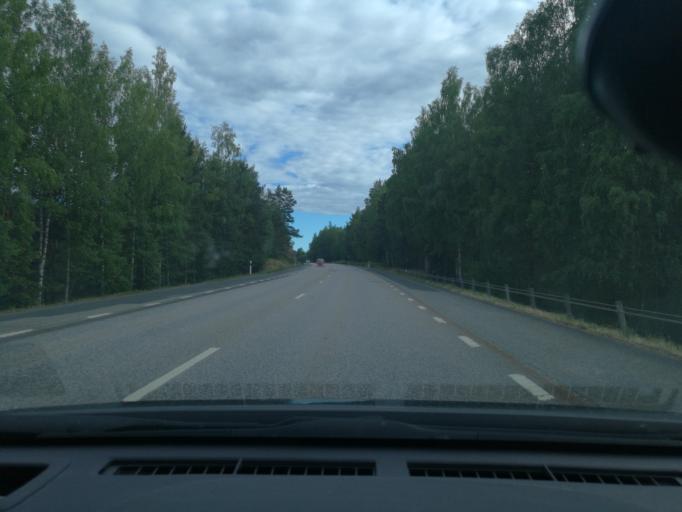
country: SE
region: Kalmar
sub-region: Vasterviks Kommun
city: Ankarsrum
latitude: 57.6908
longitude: 16.4398
